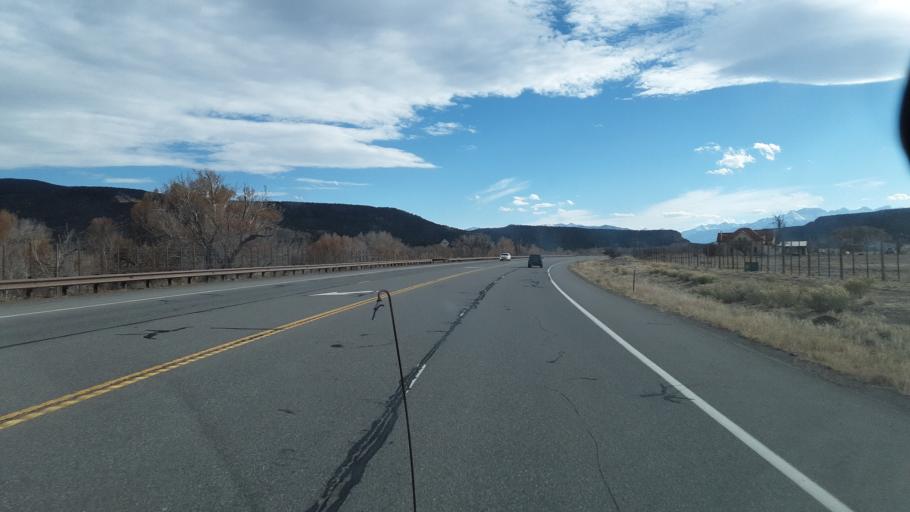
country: US
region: Colorado
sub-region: Montrose County
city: Montrose
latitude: 38.3228
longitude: -107.7769
